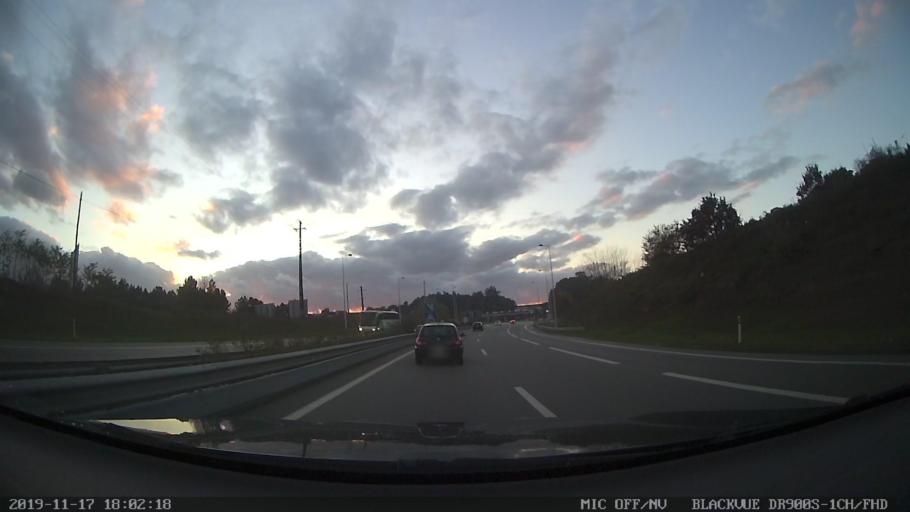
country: PT
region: Porto
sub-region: Marco de Canaveses
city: Marco de Canavezes
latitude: 41.2238
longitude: -8.1359
